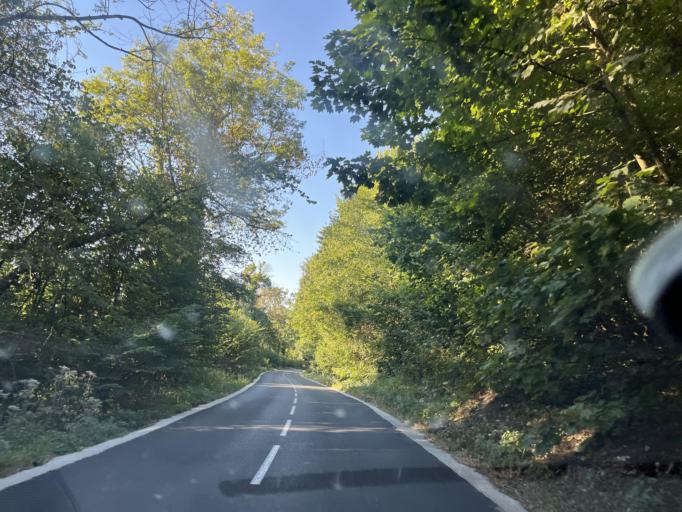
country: FR
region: Haute-Normandie
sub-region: Departement de la Seine-Maritime
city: Lillebonne
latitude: 49.5330
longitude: 0.5457
